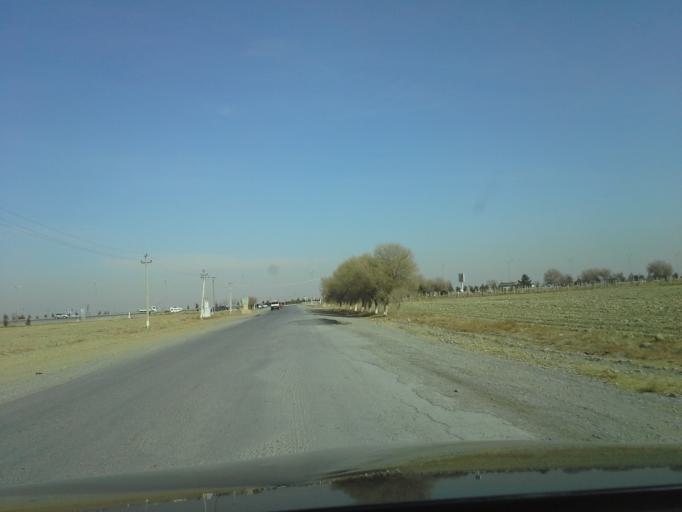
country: TM
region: Ahal
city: Abadan
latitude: 38.1344
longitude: 58.0062
